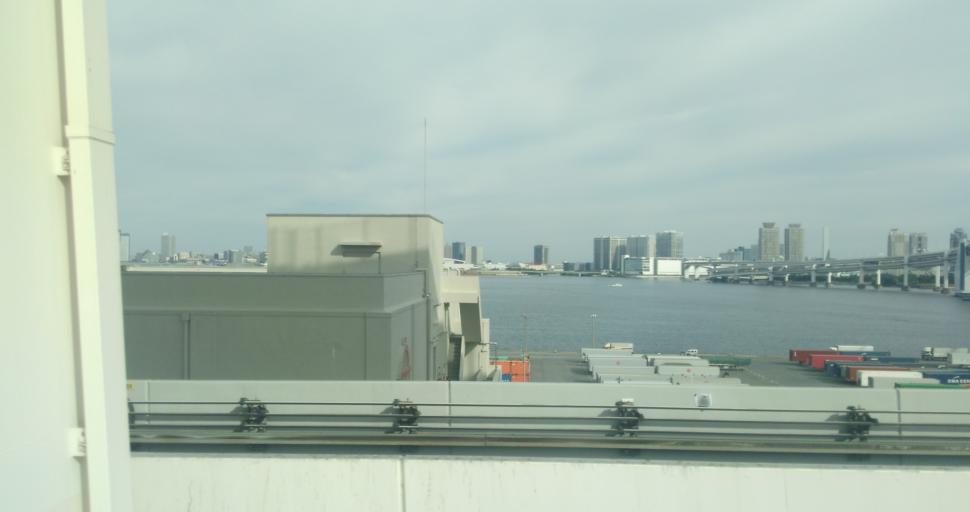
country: JP
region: Tokyo
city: Tokyo
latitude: 35.6394
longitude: 139.7579
